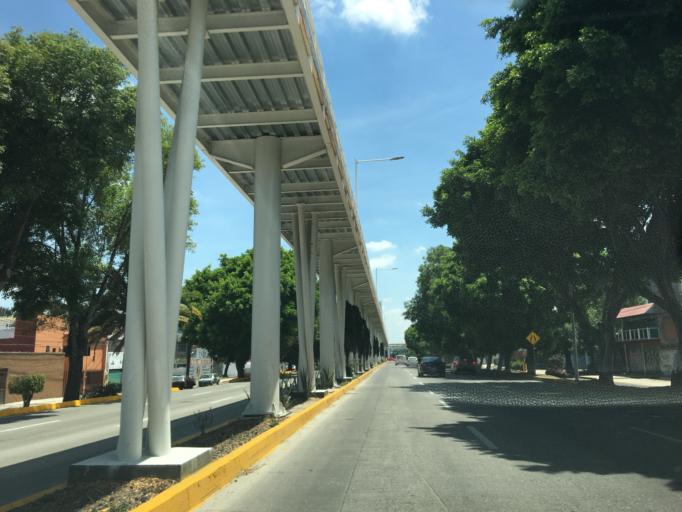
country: MX
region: Puebla
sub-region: Cuautlancingo
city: Sanctorum
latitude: 19.0880
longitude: -98.2292
